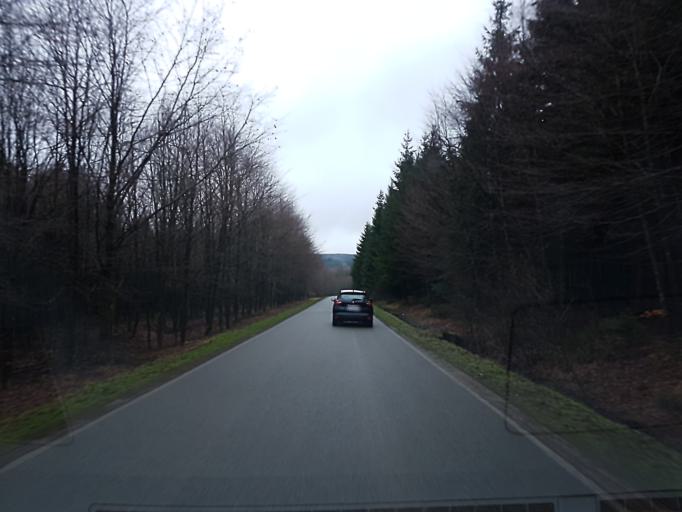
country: BE
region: Wallonia
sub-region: Province de Liege
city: Malmedy
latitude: 50.4668
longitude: 6.0444
